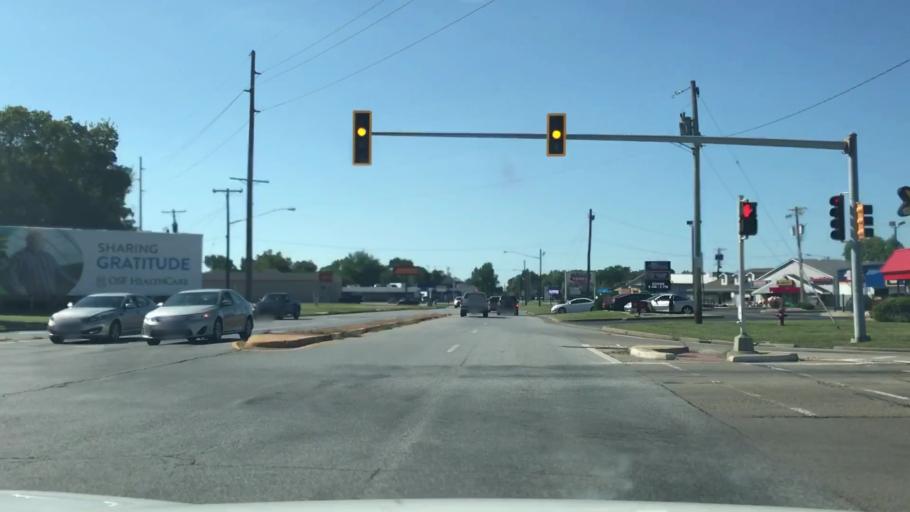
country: US
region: Illinois
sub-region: Madison County
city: Roxana
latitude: 38.8638
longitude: -90.0791
